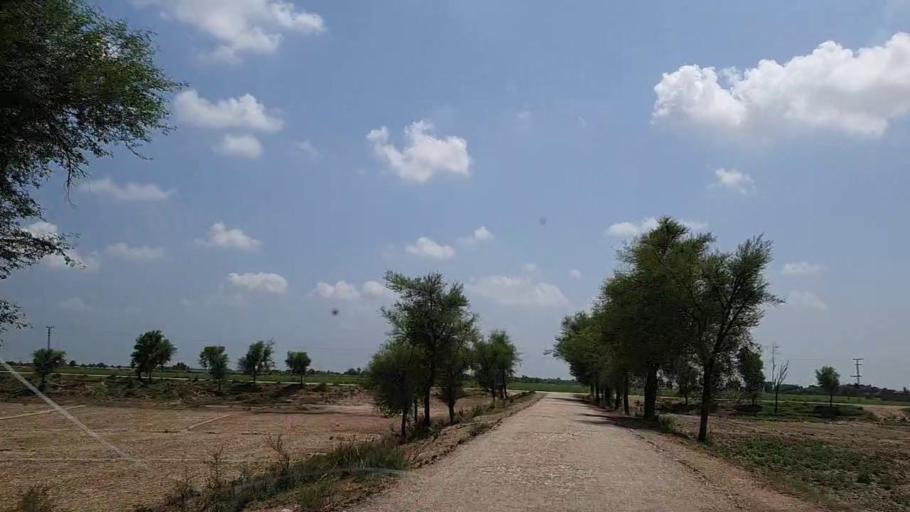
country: PK
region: Sindh
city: Tharu Shah
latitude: 27.0034
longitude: 68.0599
